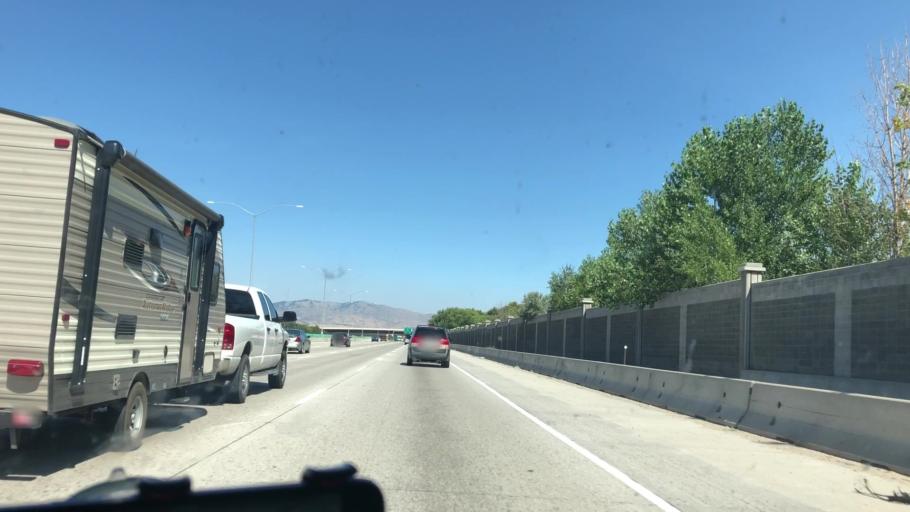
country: US
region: Idaho
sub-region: Ada County
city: Garden City
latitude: 43.5971
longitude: -116.3024
